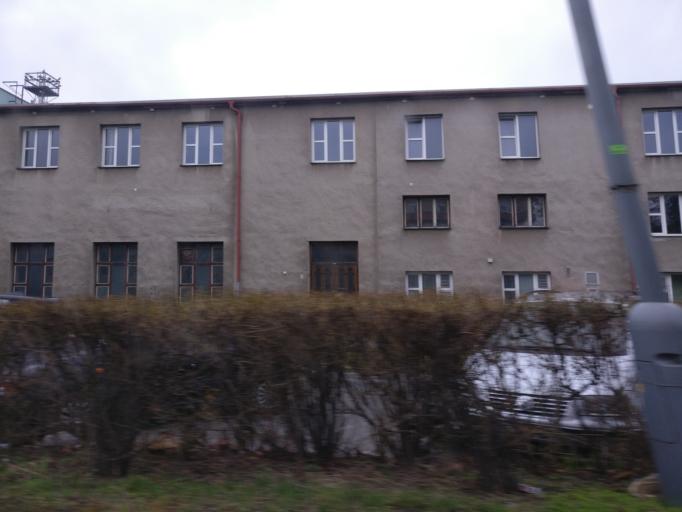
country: CZ
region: Pardubicky
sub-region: Okres Pardubice
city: Pardubice
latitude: 50.0322
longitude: 15.7651
